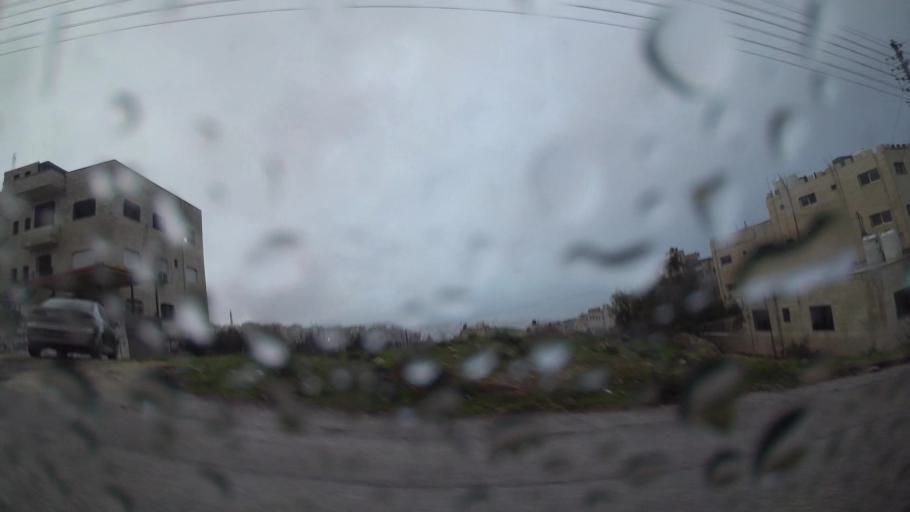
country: JO
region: Amman
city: Al Jubayhah
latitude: 32.0311
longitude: 35.8420
